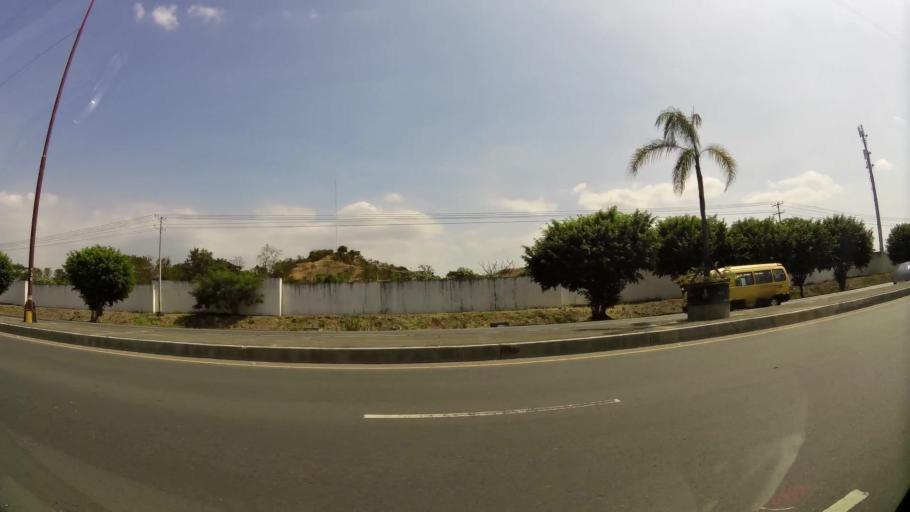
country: EC
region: Guayas
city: Eloy Alfaro
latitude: -2.0803
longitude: -79.8736
